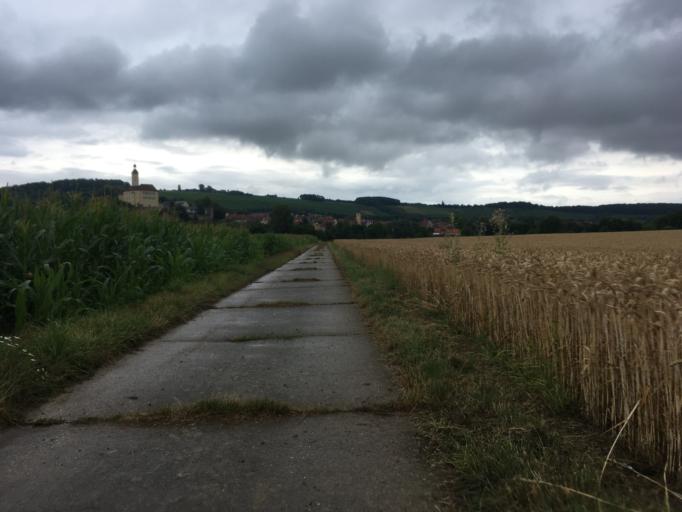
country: DE
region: Baden-Wuerttemberg
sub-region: Regierungsbezirk Stuttgart
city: Gundelsheim
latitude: 49.2837
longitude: 9.1483
